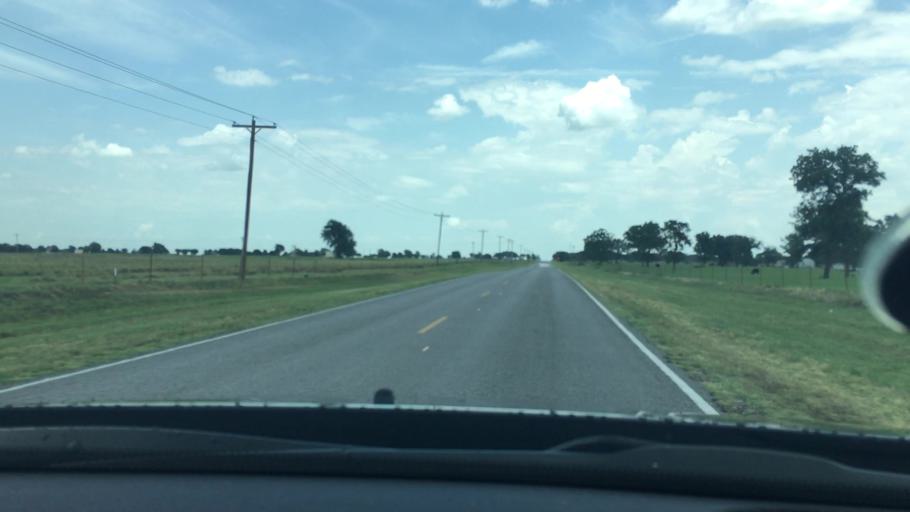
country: US
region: Oklahoma
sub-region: Carter County
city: Wilson
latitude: 33.9403
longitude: -97.3912
